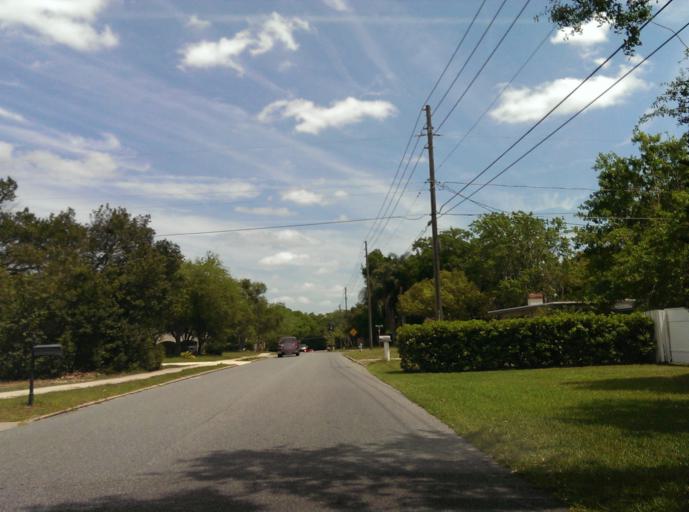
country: US
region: Florida
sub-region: Orange County
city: Doctor Phillips
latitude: 28.4827
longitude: -81.4796
